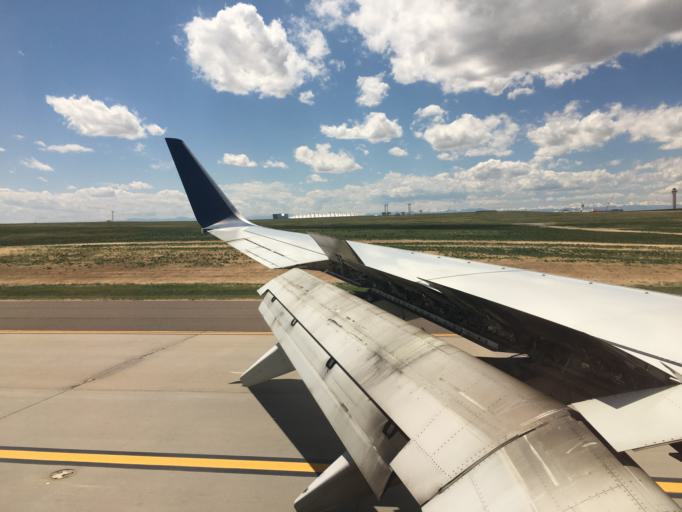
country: US
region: Colorado
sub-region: Weld County
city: Lochbuie
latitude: 39.8543
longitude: -104.6439
